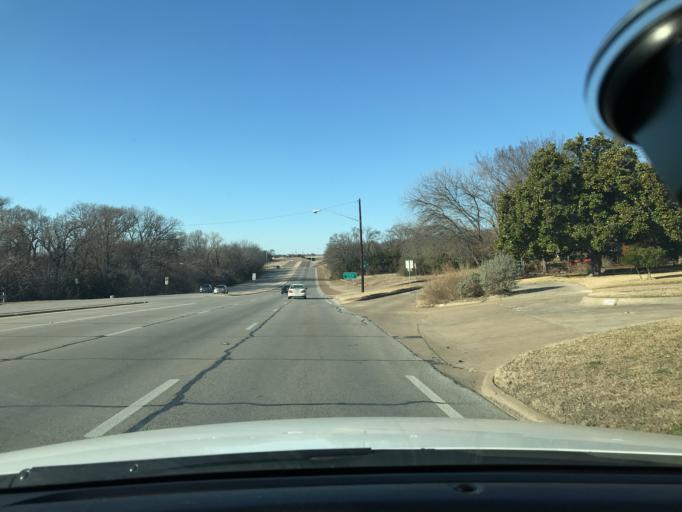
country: US
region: Texas
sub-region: Dallas County
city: Highland Park
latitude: 32.8478
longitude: -96.7144
